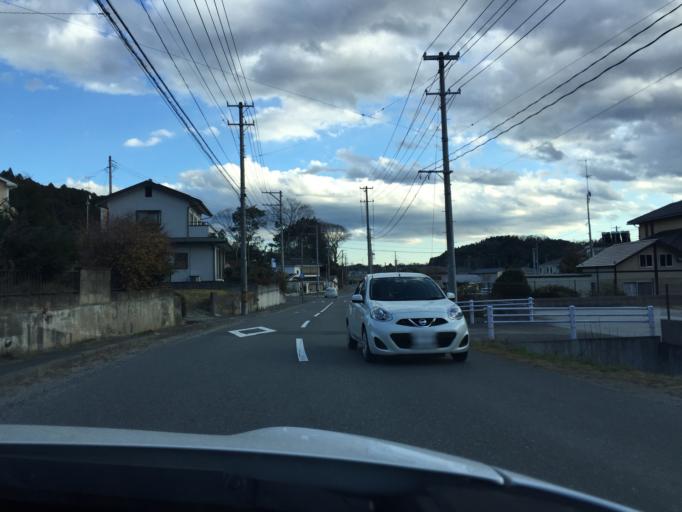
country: JP
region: Fukushima
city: Iwaki
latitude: 37.0653
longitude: 140.8655
